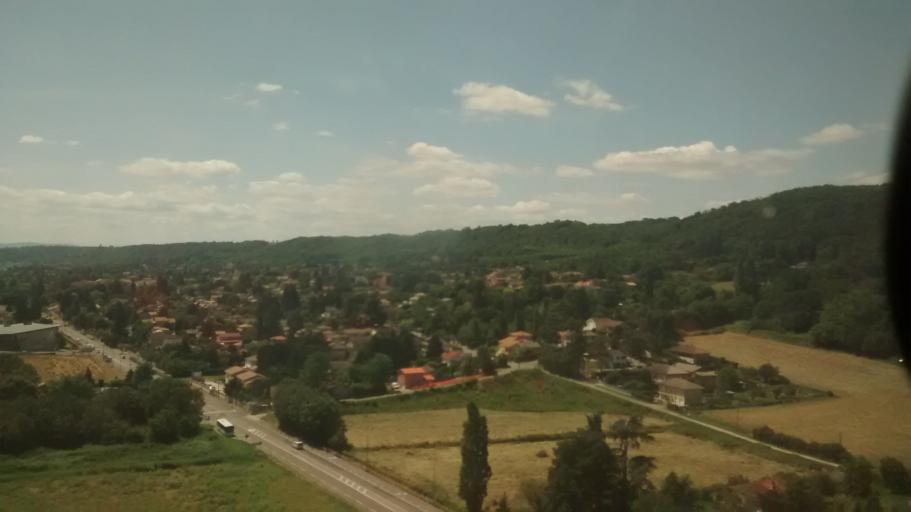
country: FR
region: Rhone-Alpes
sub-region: Departement de l'Ain
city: Beynost
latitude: 45.8386
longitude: 5.0180
